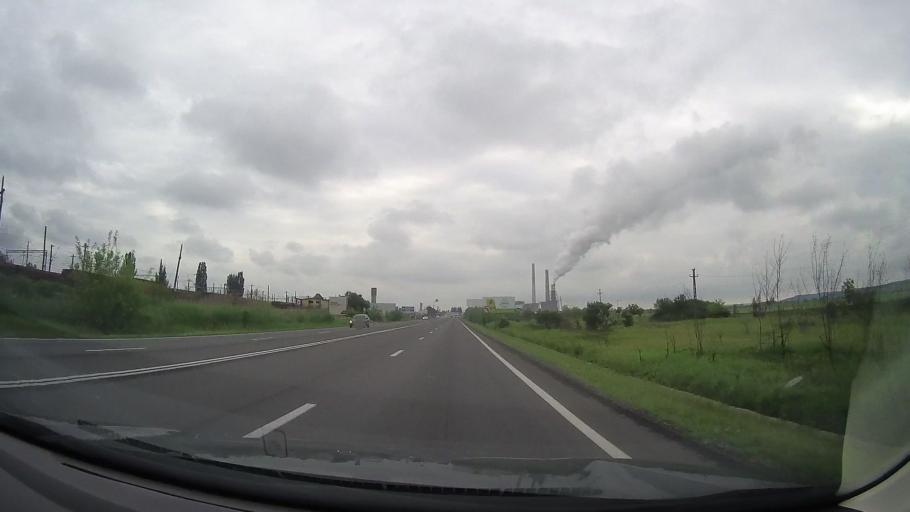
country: RO
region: Dolj
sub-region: Comuna Isalnita
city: Isalnita
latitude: 44.4041
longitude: 23.7141
